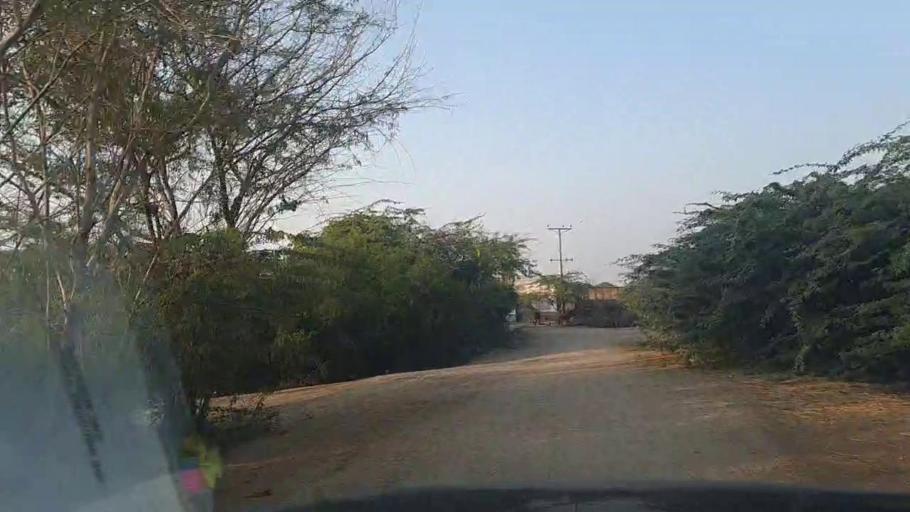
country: PK
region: Sindh
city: Keti Bandar
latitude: 24.3169
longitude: 67.5993
